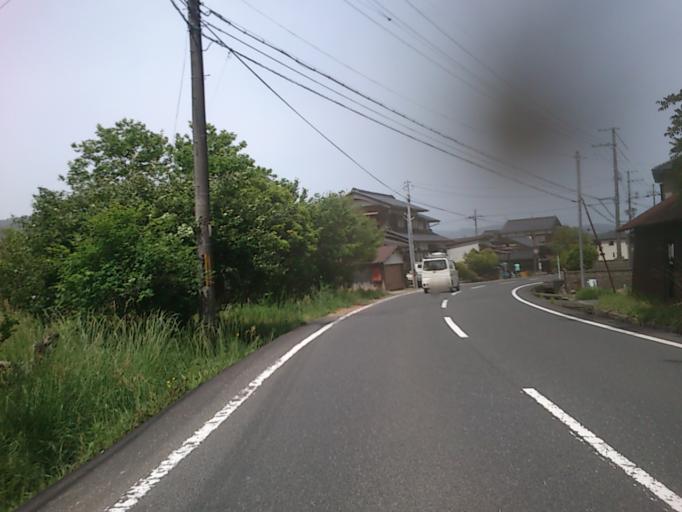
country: JP
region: Kyoto
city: Miyazu
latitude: 35.5751
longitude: 135.1025
